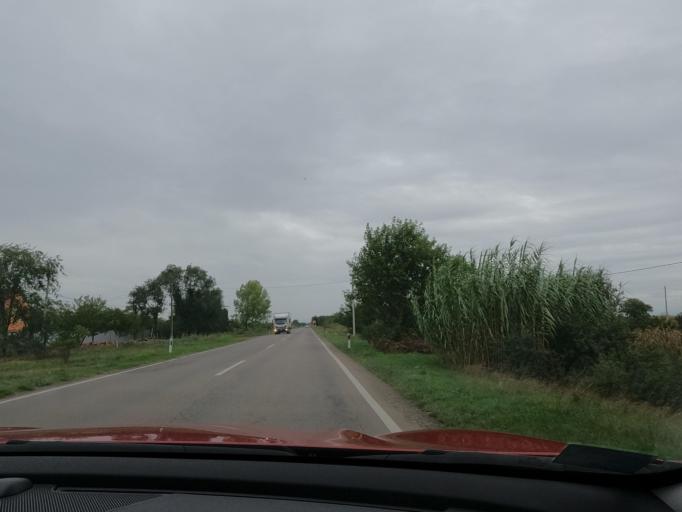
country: RS
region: Autonomna Pokrajina Vojvodina
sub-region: Severnobanatski Okrug
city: Kikinda
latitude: 45.7836
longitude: 20.4314
